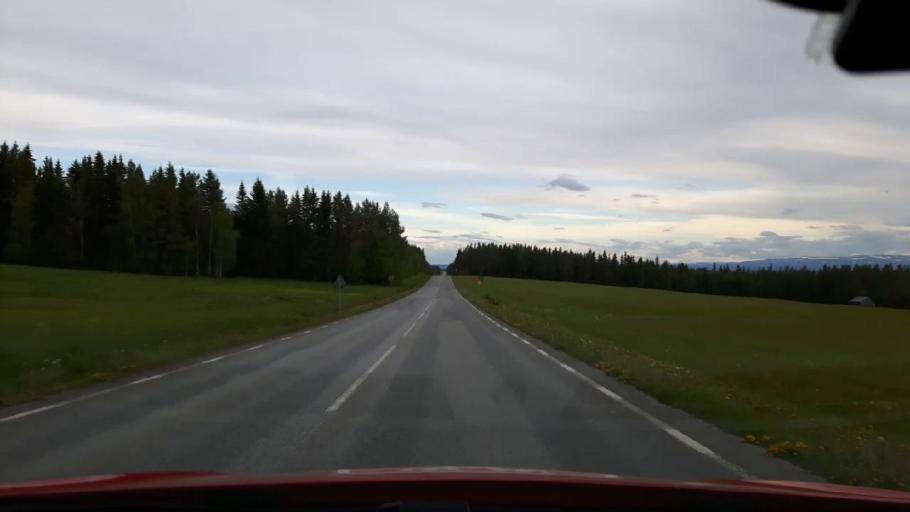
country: SE
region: Jaemtland
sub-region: OEstersunds Kommun
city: Ostersund
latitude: 63.1494
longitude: 14.4831
